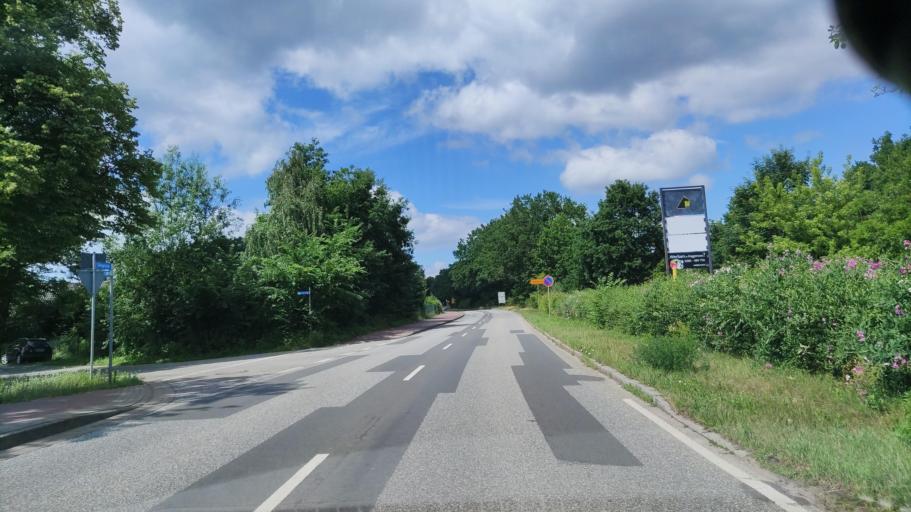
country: DE
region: Mecklenburg-Vorpommern
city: Hagenow
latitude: 53.4331
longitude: 11.1810
